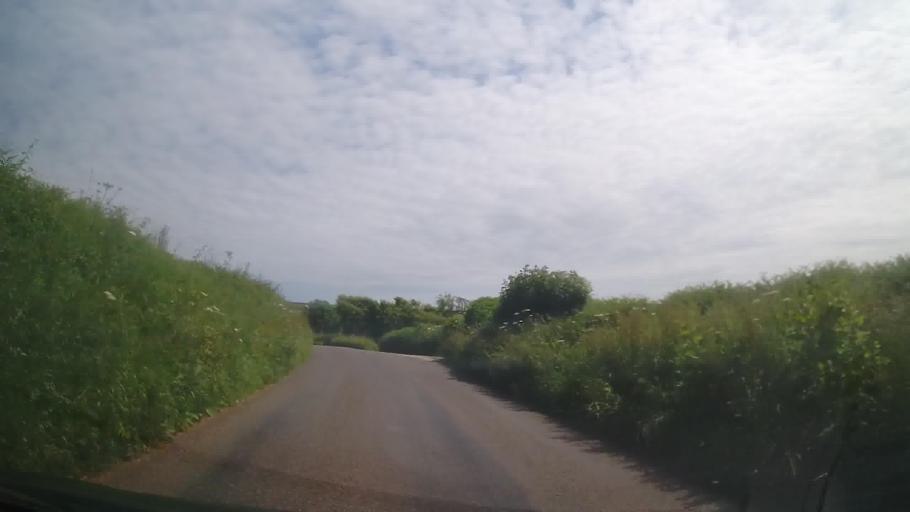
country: GB
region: England
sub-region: Devon
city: Salcombe
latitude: 50.2698
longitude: -3.6796
